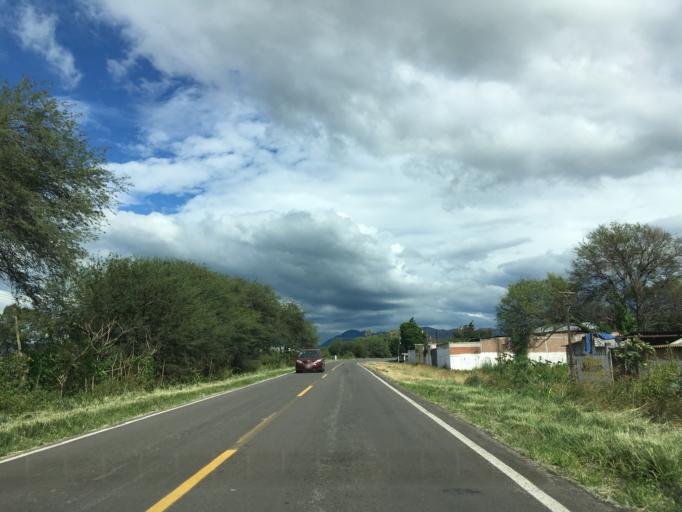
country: MX
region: Michoacan
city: Santa Ana Maya
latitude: 20.0444
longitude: -101.0669
